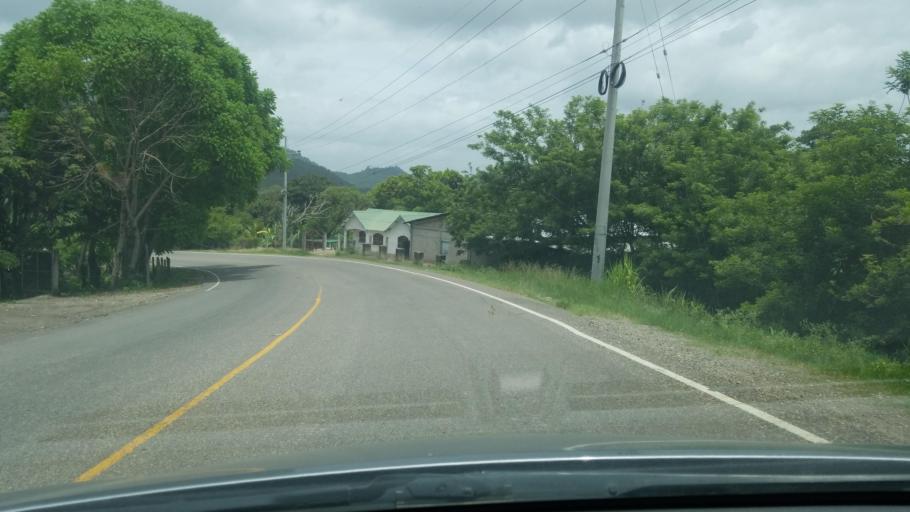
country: HN
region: Copan
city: Ojos de Agua
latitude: 14.6805
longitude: -88.8212
